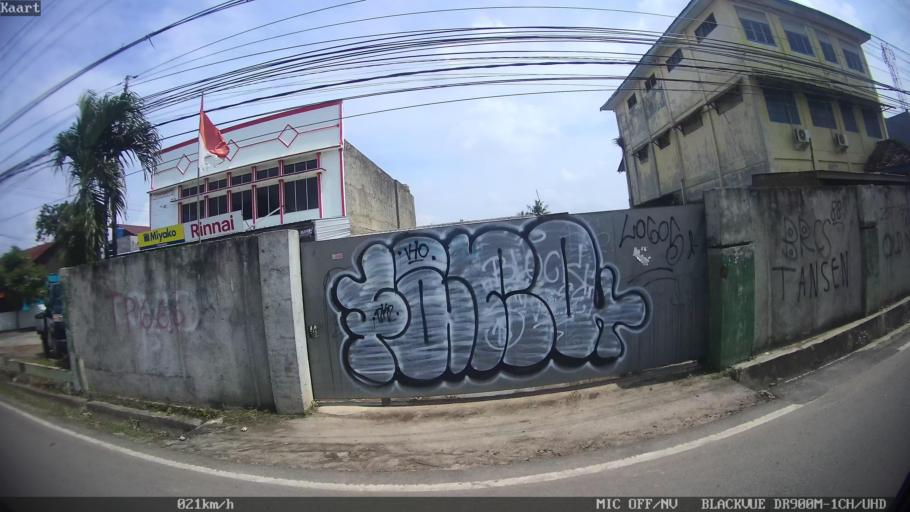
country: ID
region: Lampung
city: Kedaton
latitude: -5.3631
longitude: 105.2792
